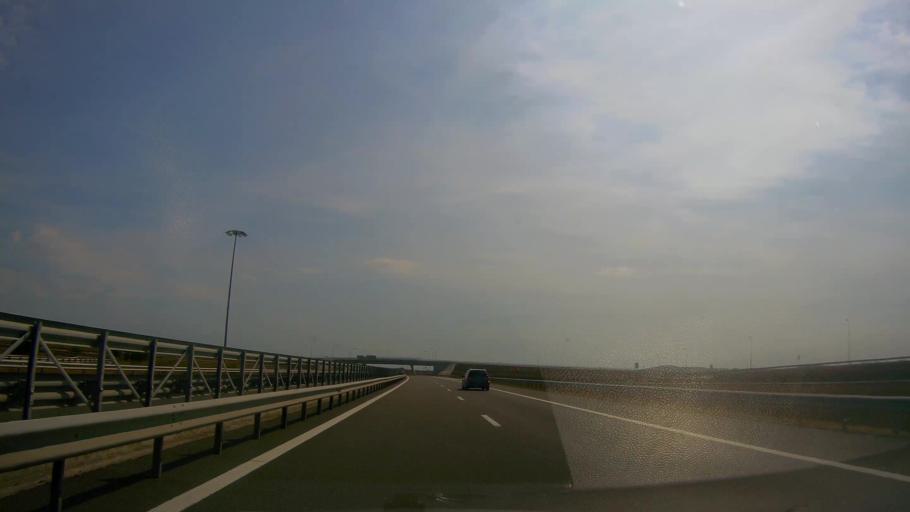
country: RO
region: Cluj
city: Turda
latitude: 46.5272
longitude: 23.7921
